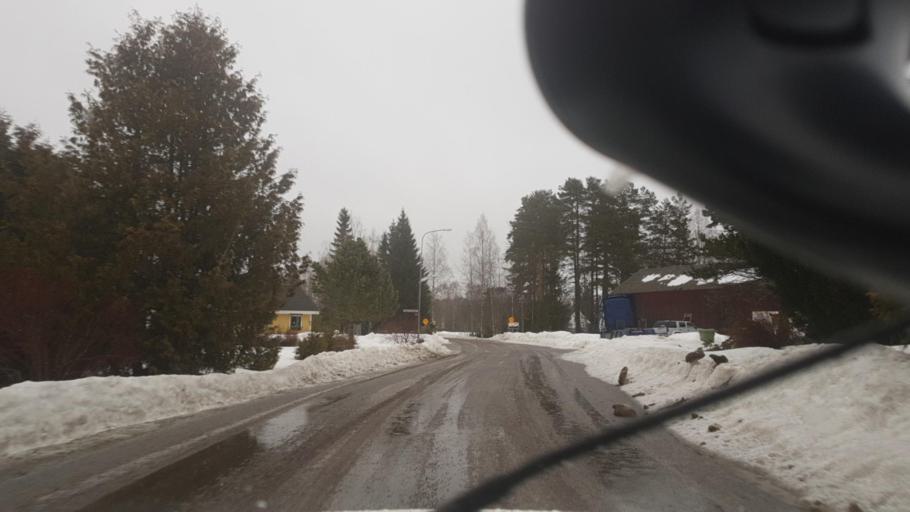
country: SE
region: Vaermland
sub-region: Eda Kommun
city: Charlottenberg
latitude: 59.8905
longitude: 12.3059
